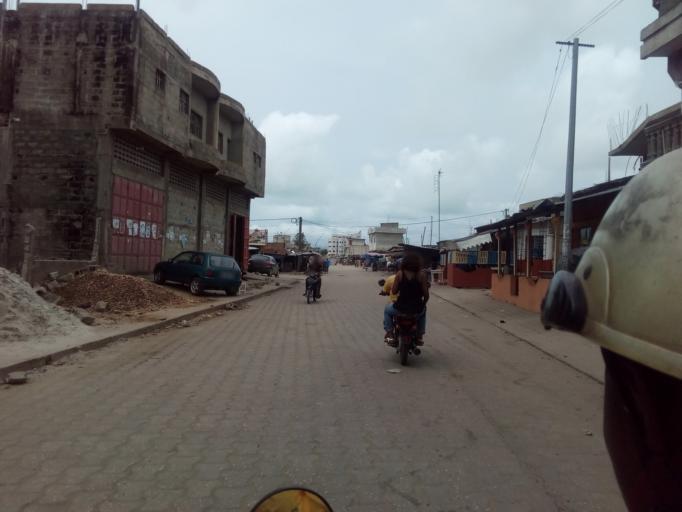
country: BJ
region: Littoral
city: Cotonou
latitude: 6.3758
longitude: 2.4392
